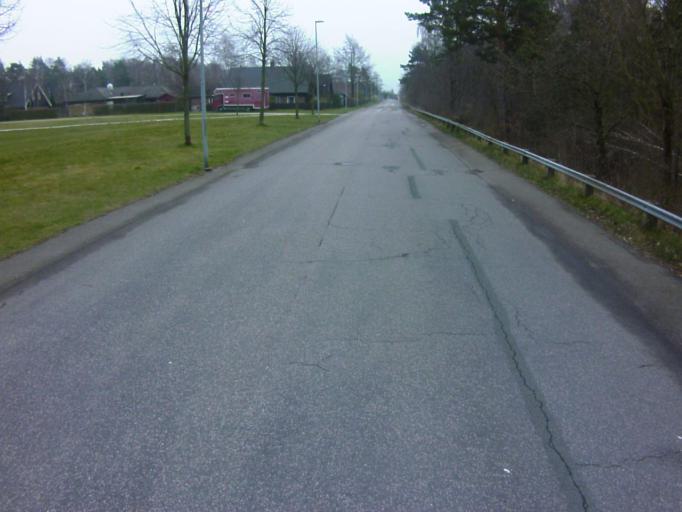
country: SE
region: Skane
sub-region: Kavlinge Kommun
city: Kaevlinge
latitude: 55.7756
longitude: 13.0796
